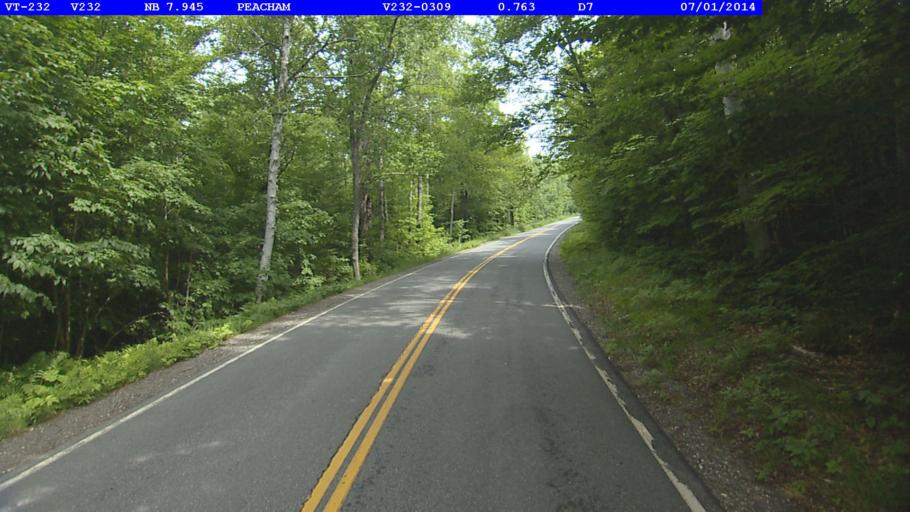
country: US
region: Vermont
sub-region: Caledonia County
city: Hardwick
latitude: 44.3064
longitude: -72.3033
